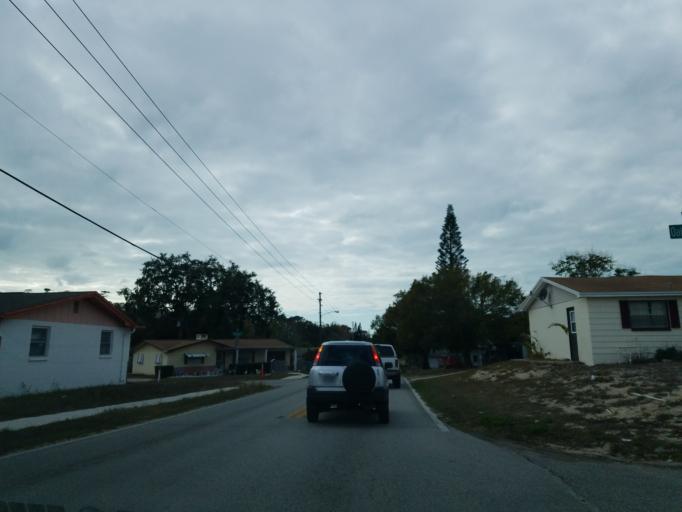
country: US
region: Florida
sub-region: Pasco County
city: Beacon Square
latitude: 28.2096
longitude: -82.7468
